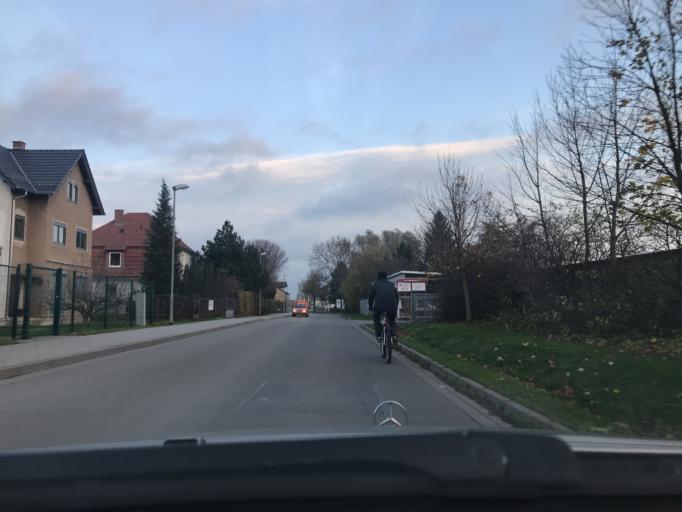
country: DE
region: Thuringia
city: Muehlhausen
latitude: 51.2104
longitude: 10.4750
